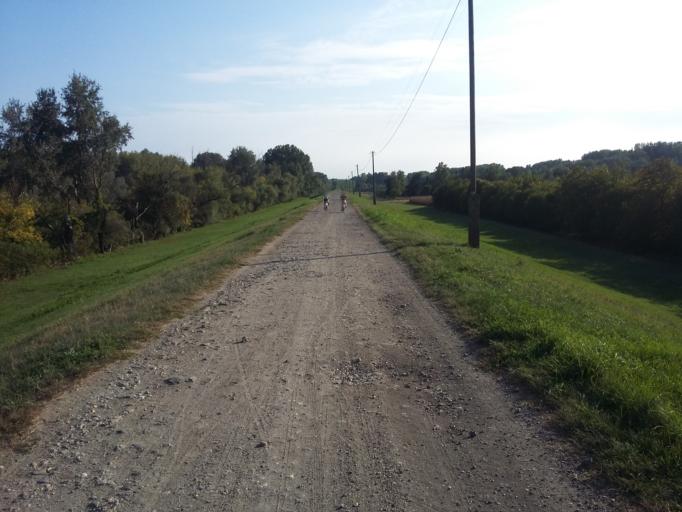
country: HU
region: Csongrad
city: Szeged
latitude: 46.2150
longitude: 20.1206
